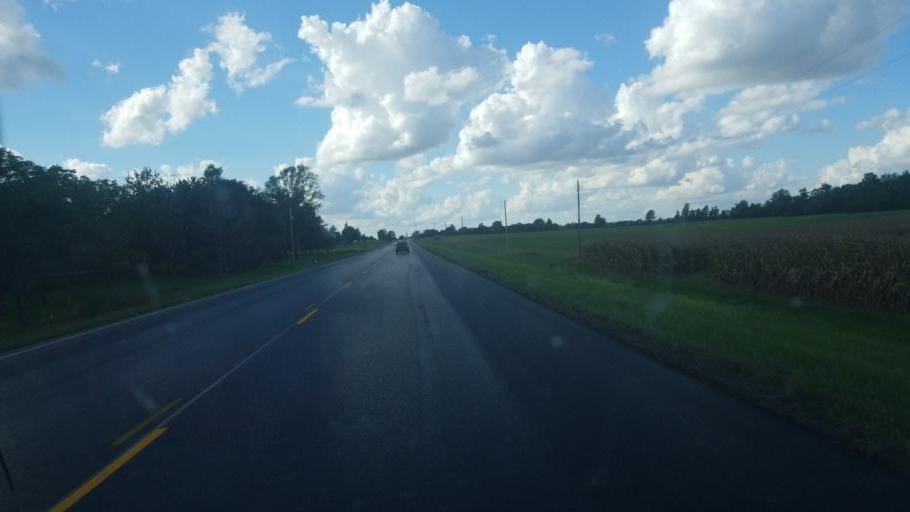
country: US
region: Ohio
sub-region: Hardin County
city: Kenton
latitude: 40.6824
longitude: -83.6799
